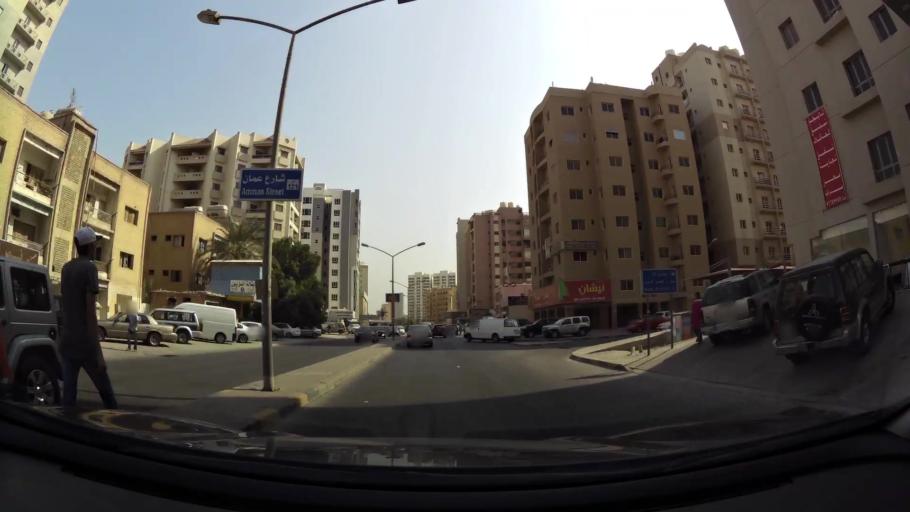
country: KW
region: Muhafazat Hawalli
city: As Salimiyah
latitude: 29.3299
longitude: 48.0549
